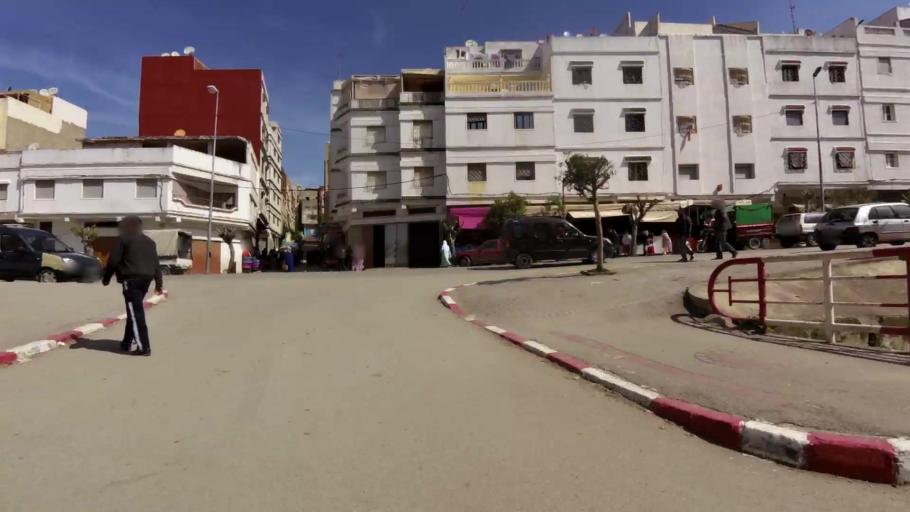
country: MA
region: Tanger-Tetouan
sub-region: Tanger-Assilah
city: Tangier
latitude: 35.7369
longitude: -5.8036
